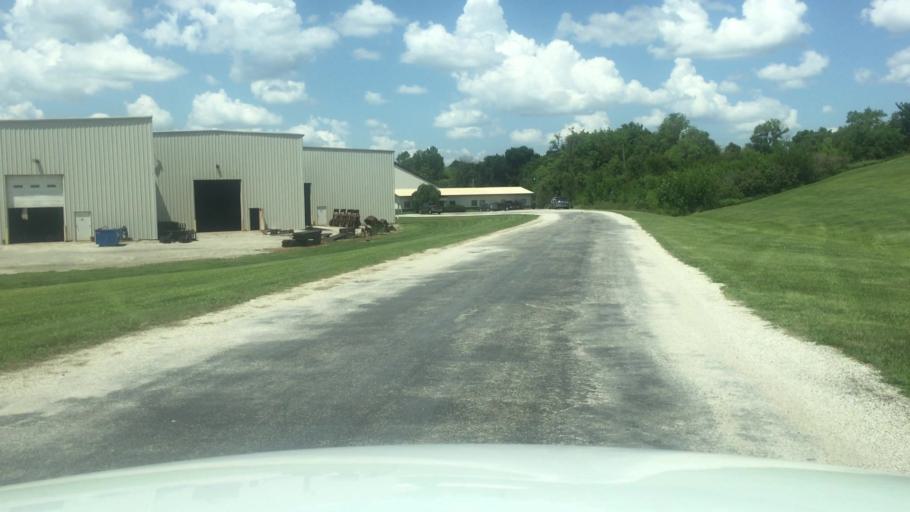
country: US
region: Kansas
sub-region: Brown County
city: Horton
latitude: 39.6560
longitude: -95.5281
